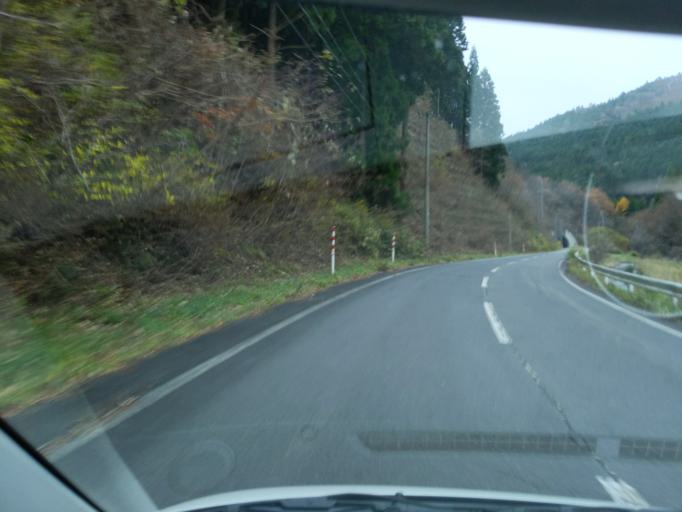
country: JP
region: Iwate
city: Mizusawa
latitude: 39.0905
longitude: 141.3861
